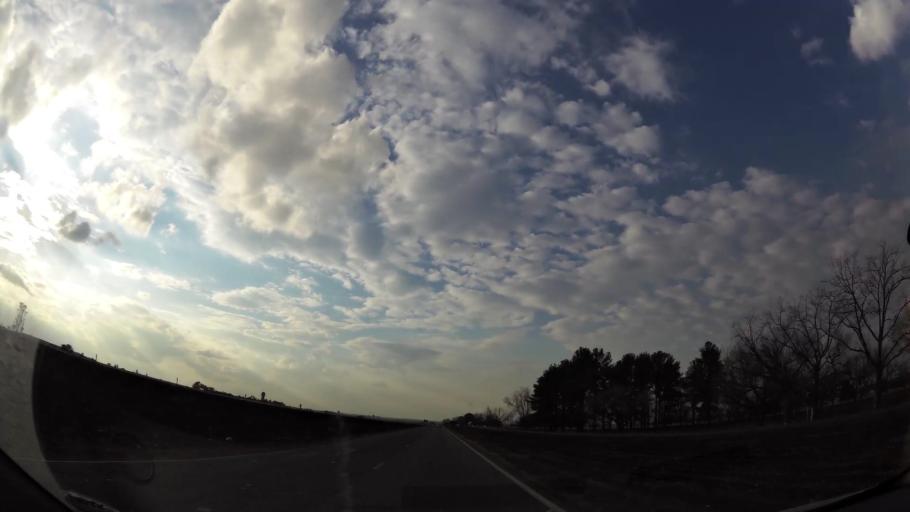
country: ZA
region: Orange Free State
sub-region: Fezile Dabi District Municipality
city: Sasolburg
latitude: -26.7795
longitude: 27.8244
